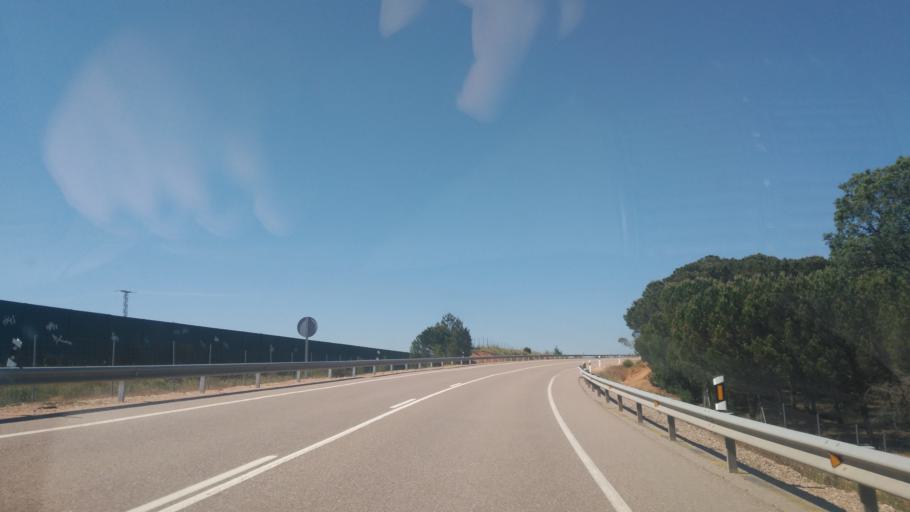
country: ES
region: Castille and Leon
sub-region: Provincia de Zamora
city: Cuelgamures
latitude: 41.2338
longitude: -5.7049
